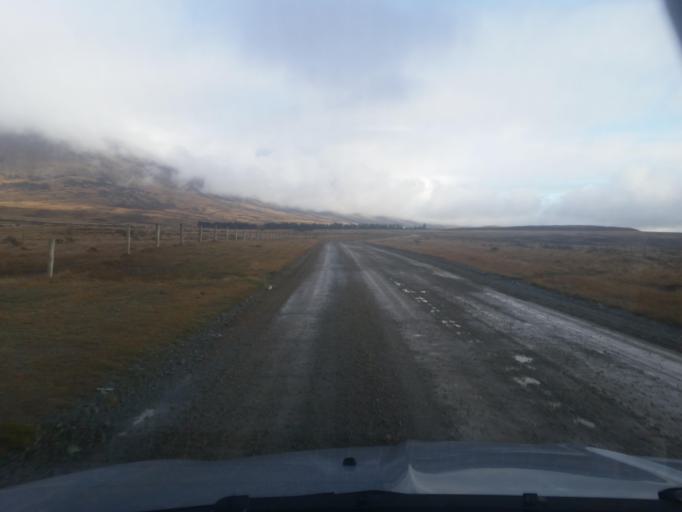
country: NZ
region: Canterbury
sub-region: Ashburton District
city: Methven
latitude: -43.6168
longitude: 171.0838
